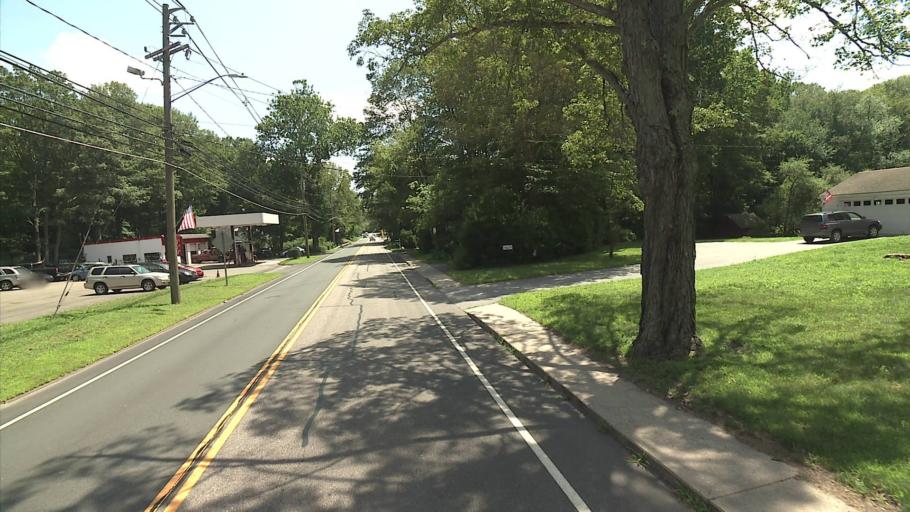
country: US
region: Connecticut
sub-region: Middlesex County
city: Deep River Center
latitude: 41.3730
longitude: -72.4299
